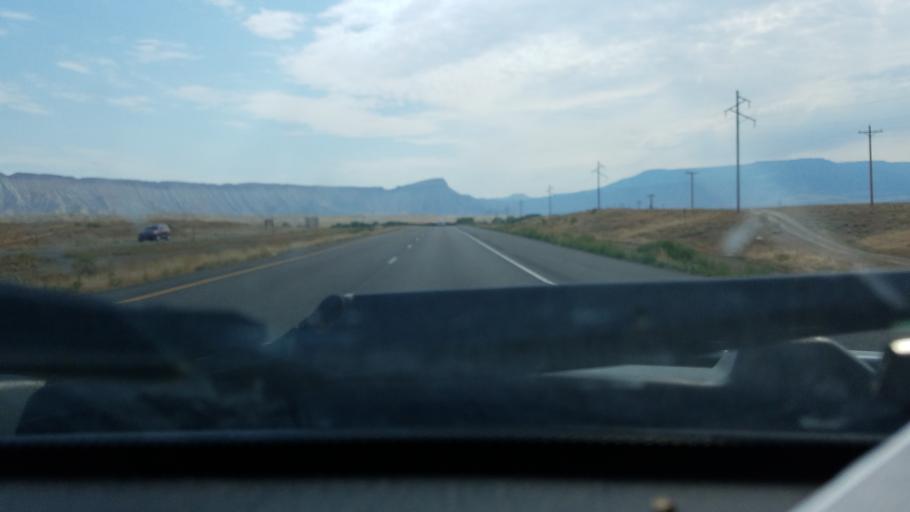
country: US
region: Colorado
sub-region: Mesa County
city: Fruitvale
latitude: 39.1065
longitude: -108.5202
